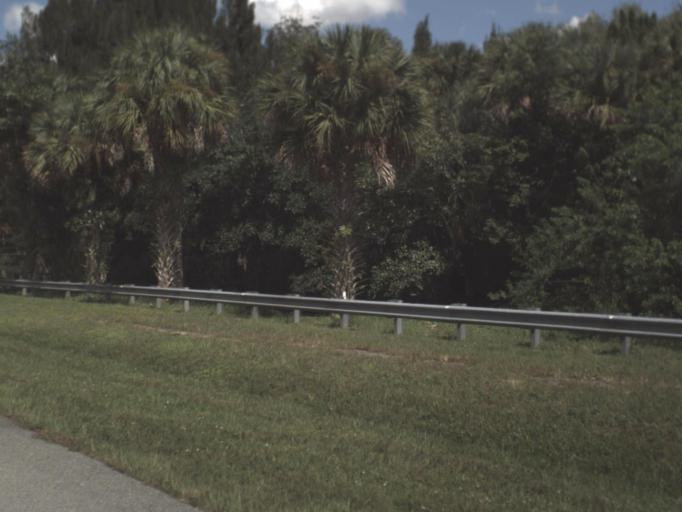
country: US
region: Florida
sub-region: Collier County
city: Immokalee
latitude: 26.2656
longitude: -81.3420
